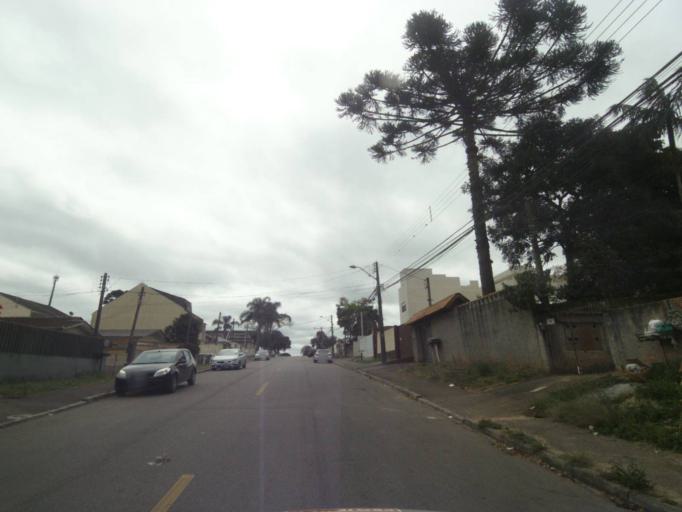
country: BR
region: Parana
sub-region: Sao Jose Dos Pinhais
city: Sao Jose dos Pinhais
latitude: -25.4837
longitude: -49.2304
